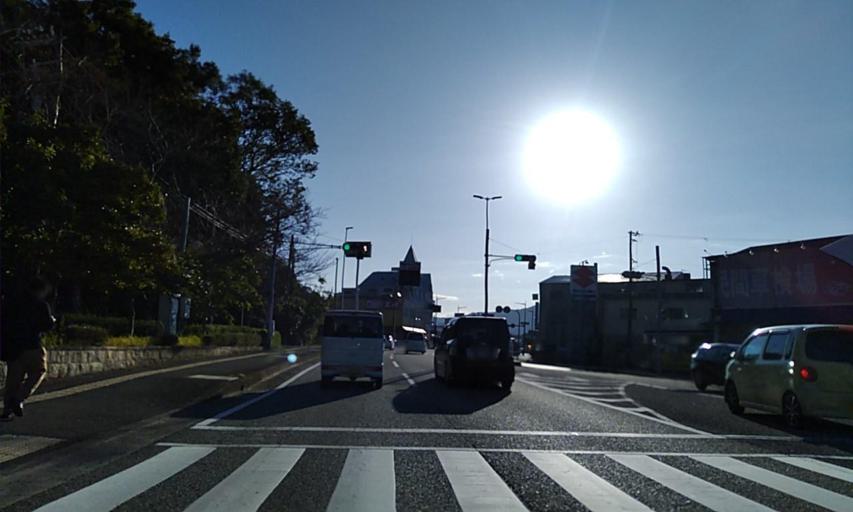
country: JP
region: Wakayama
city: Kainan
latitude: 34.1605
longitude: 135.1917
